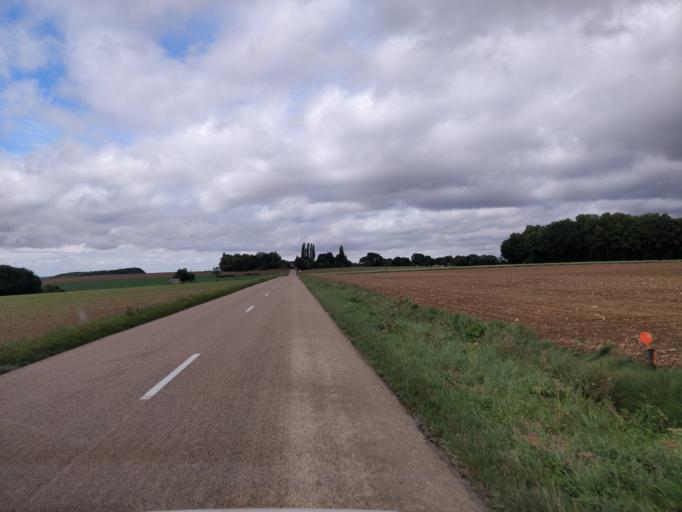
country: FR
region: Champagne-Ardenne
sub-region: Departement de l'Aube
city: Aix-en-Othe
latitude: 48.1224
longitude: 3.6673
